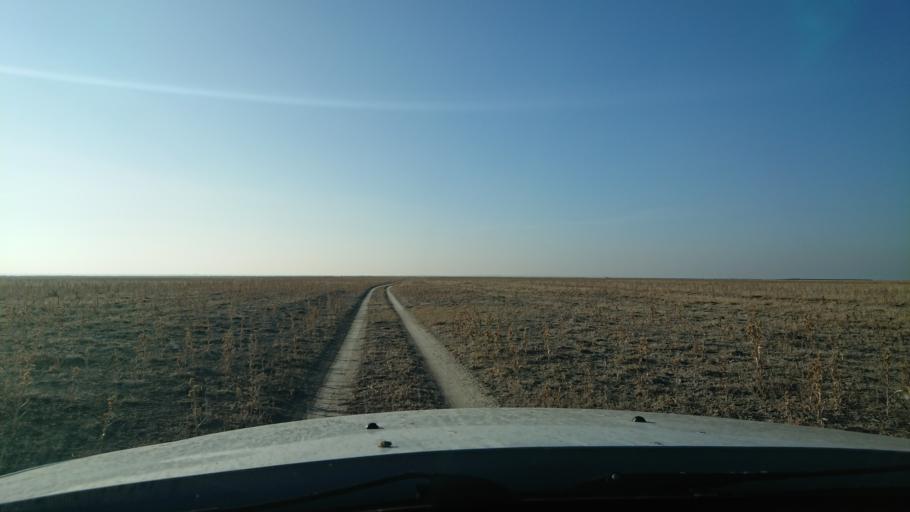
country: TR
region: Aksaray
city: Sultanhani
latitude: 38.3719
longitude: 33.5435
